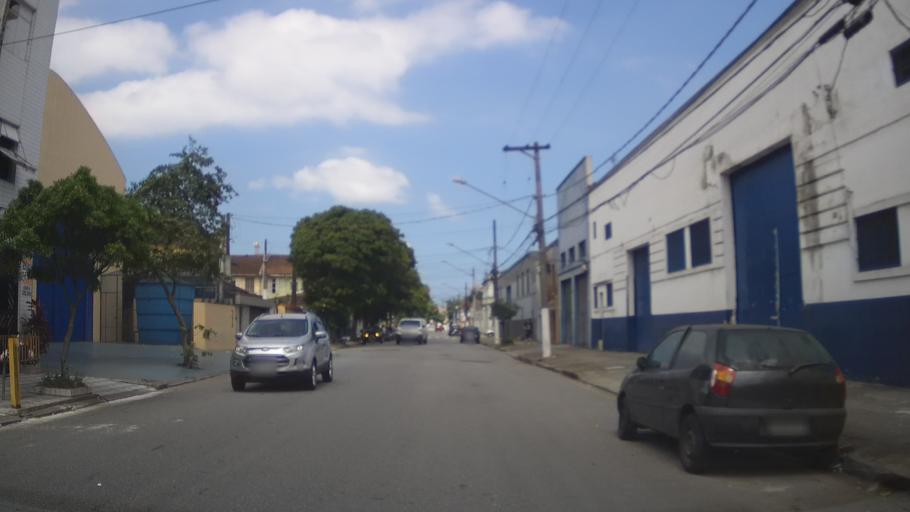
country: BR
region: Sao Paulo
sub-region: Santos
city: Santos
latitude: -23.9541
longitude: -46.3185
